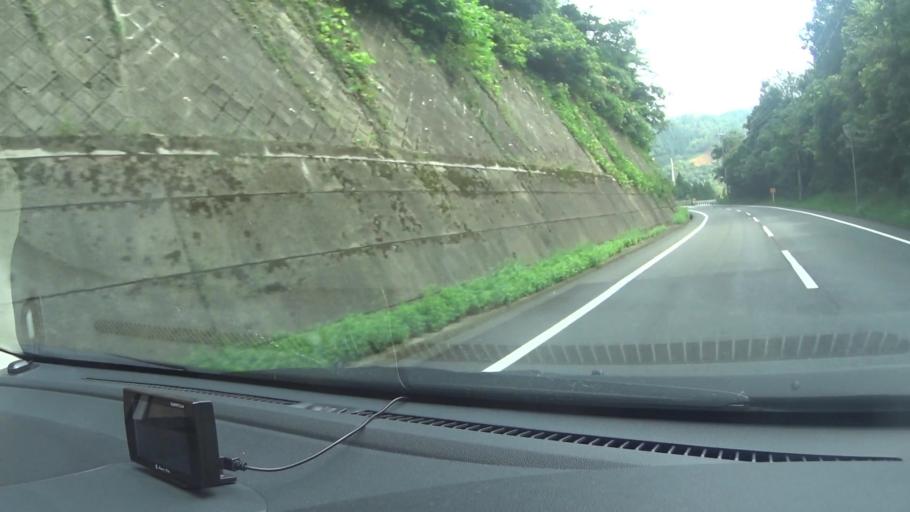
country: JP
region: Kyoto
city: Ayabe
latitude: 35.2781
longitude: 135.2663
